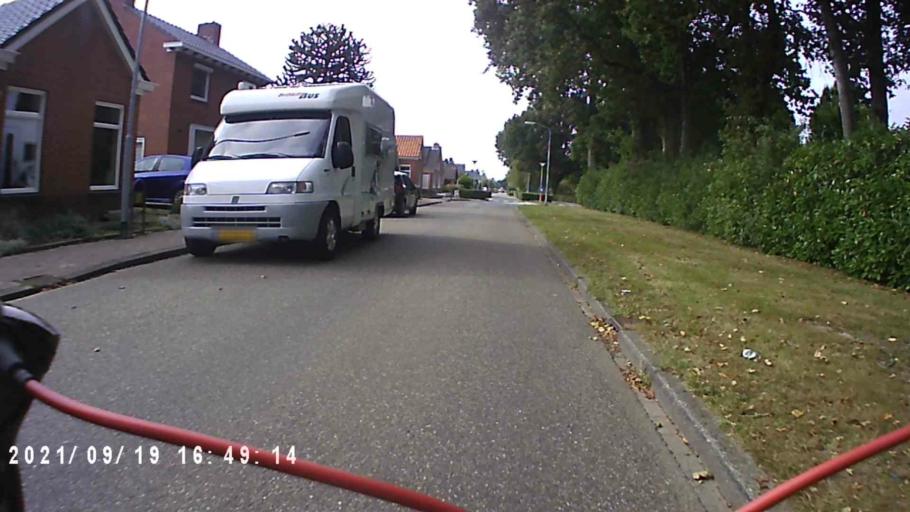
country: NL
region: Groningen
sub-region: Gemeente  Oldambt
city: Winschoten
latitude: 53.1759
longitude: 7.0940
